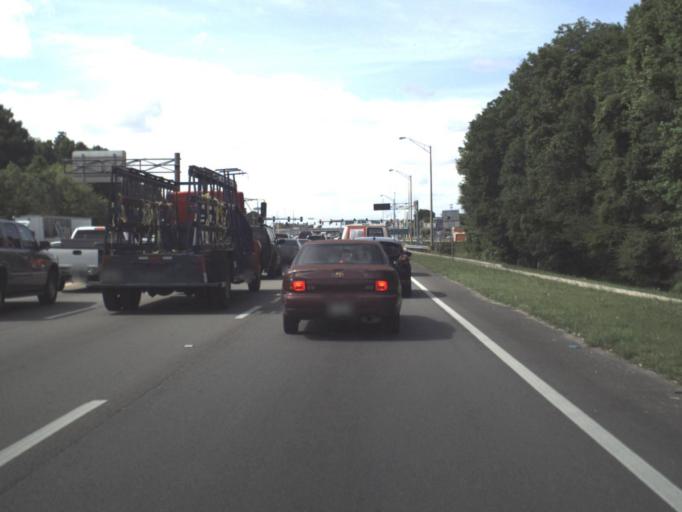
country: US
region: Florida
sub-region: Clay County
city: Bellair-Meadowbrook Terrace
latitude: 30.1897
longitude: -81.7392
